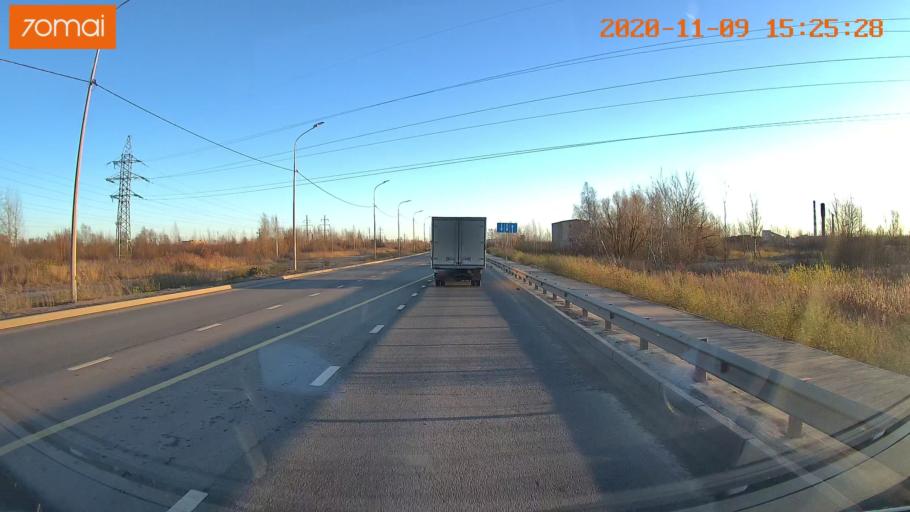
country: RU
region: Ivanovo
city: Novo-Talitsy
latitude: 56.9834
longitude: 40.9130
